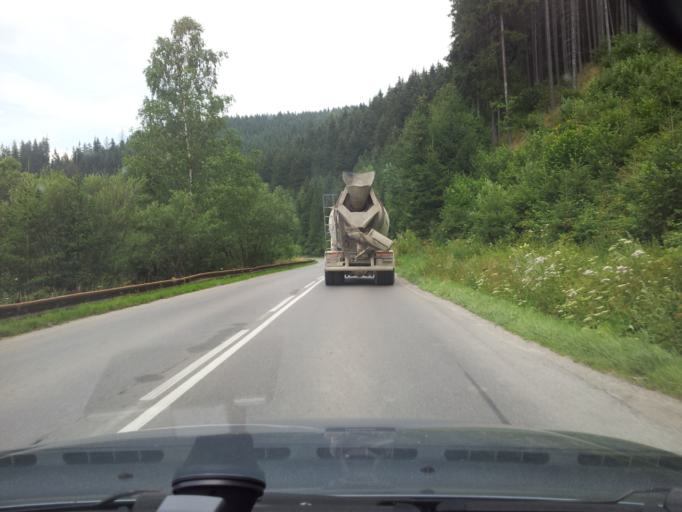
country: SK
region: Zilinsky
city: Namestovo
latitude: 49.3821
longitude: 19.3894
